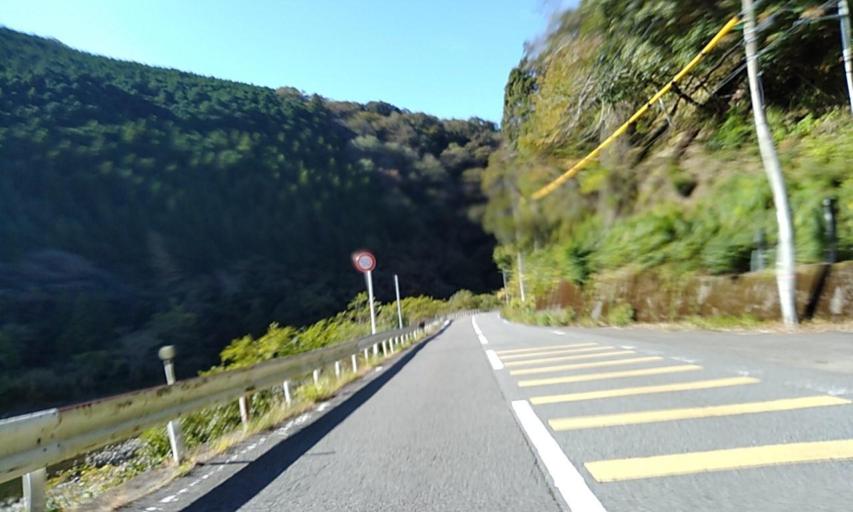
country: JP
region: Wakayama
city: Kainan
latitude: 34.0615
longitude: 135.3578
